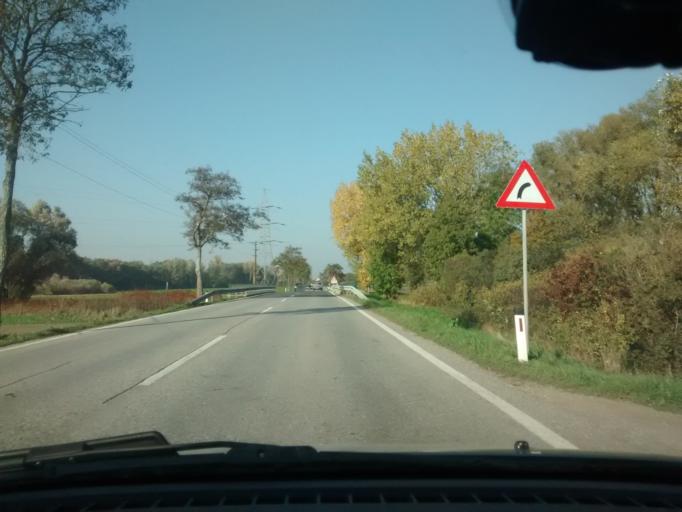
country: AT
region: Lower Austria
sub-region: Politischer Bezirk Modling
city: Achau
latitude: 48.0645
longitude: 16.3821
